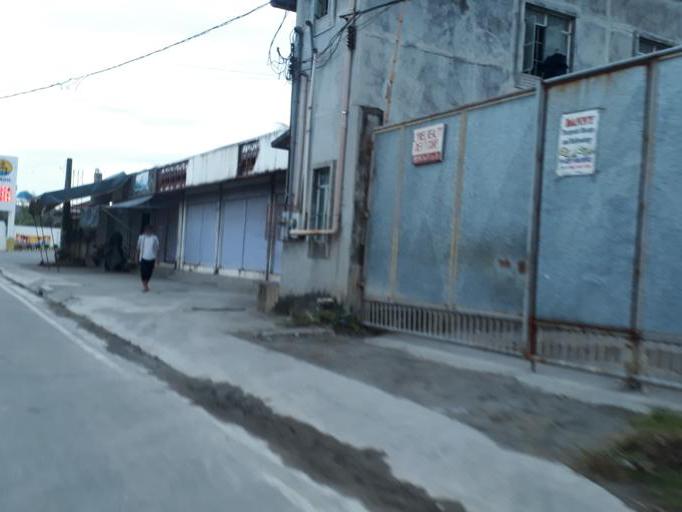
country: PH
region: Calabarzon
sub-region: Province of Rizal
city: Valenzuela
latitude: 14.7011
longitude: 120.9503
